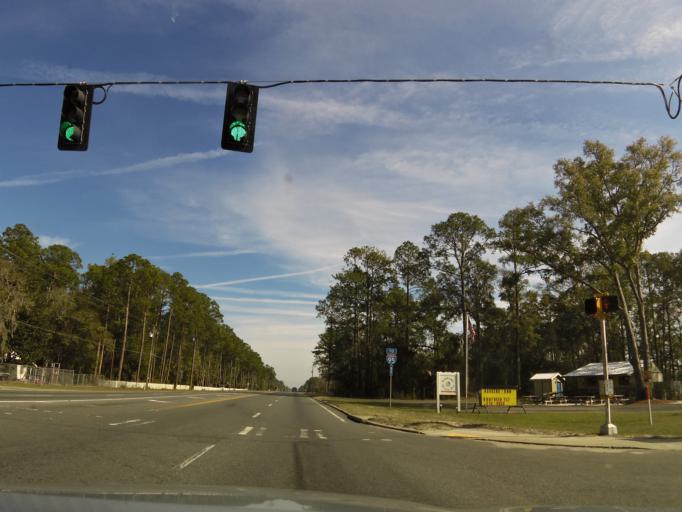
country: US
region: Georgia
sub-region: Brantley County
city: Nahunta
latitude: 31.2217
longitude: -81.8529
